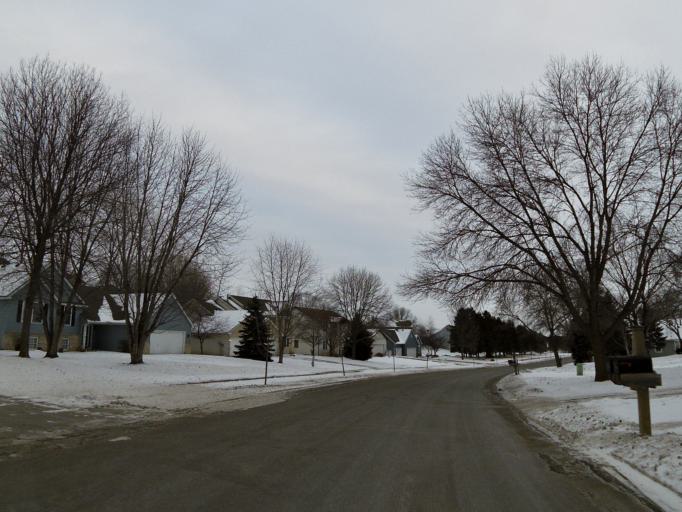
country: US
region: Minnesota
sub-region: Washington County
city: Woodbury
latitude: 44.9145
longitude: -92.9160
